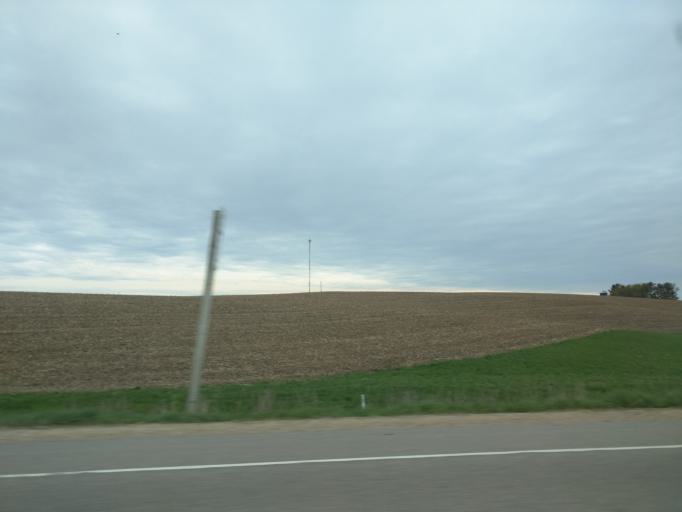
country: US
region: Minnesota
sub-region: Goodhue County
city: Red Wing
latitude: 44.5891
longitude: -92.3995
